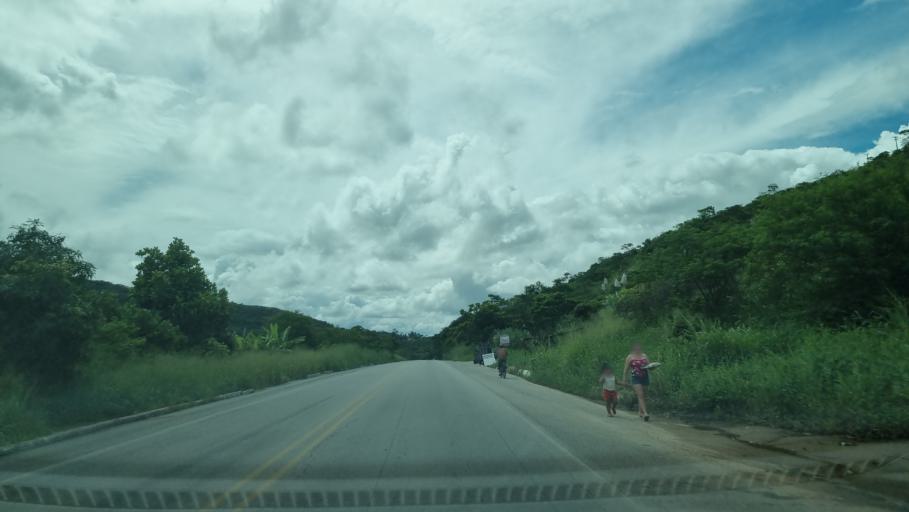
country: BR
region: Pernambuco
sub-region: Caruaru
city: Caruaru
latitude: -8.3622
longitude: -35.9862
